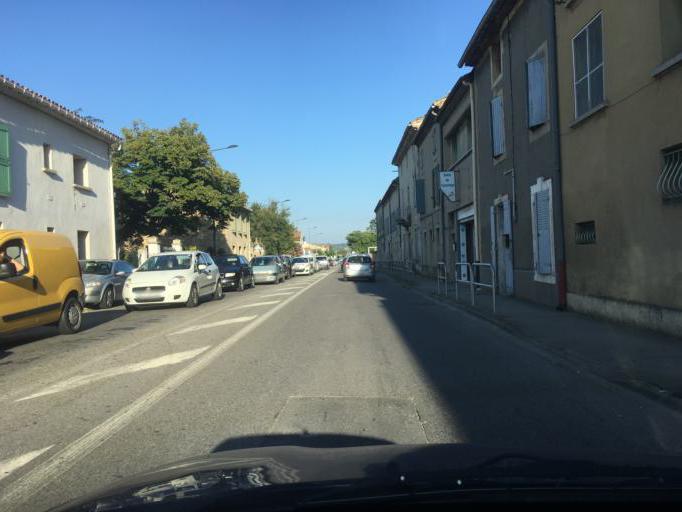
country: FR
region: Languedoc-Roussillon
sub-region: Departement du Gard
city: Remoulins
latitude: 43.9389
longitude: 4.5650
